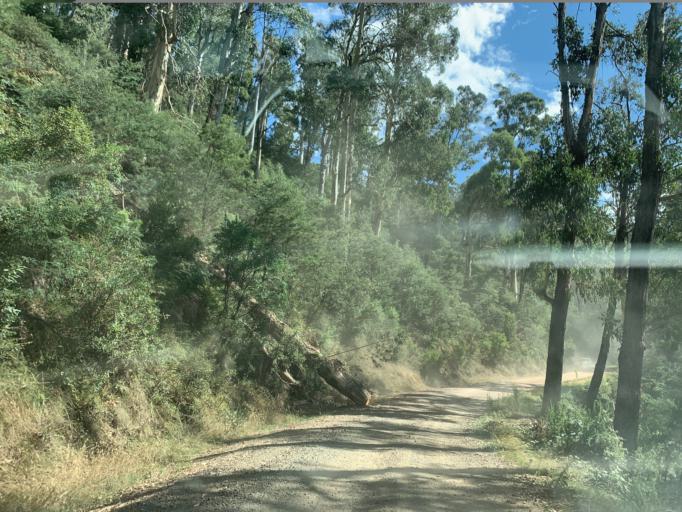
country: AU
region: Victoria
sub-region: Mansfield
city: Mansfield
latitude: -37.0944
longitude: 146.5269
